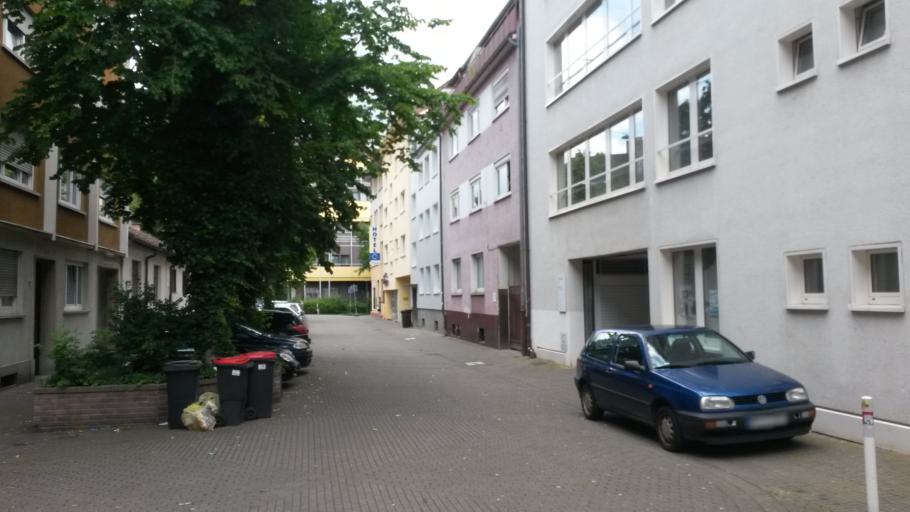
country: DE
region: Baden-Wuerttemberg
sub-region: Karlsruhe Region
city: Pforzheim
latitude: 48.8954
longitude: 8.7023
